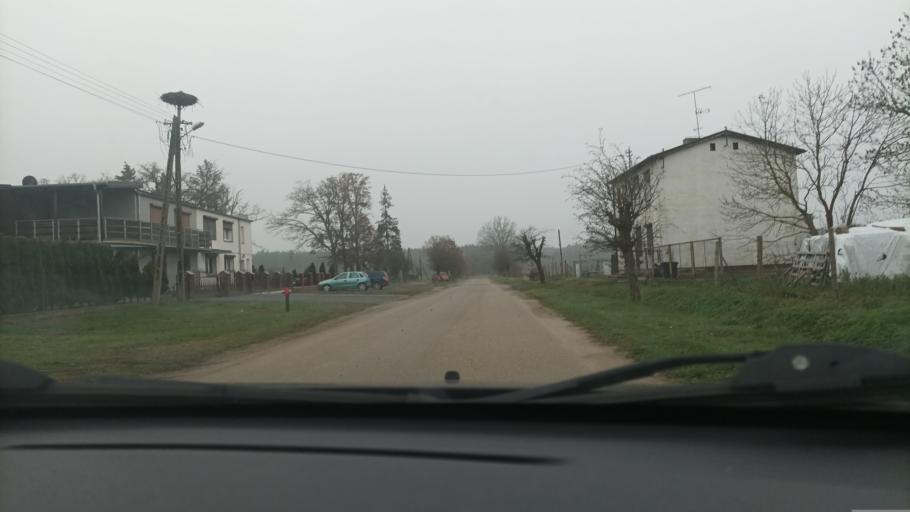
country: PL
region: Greater Poland Voivodeship
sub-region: Powiat obornicki
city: Ryczywol
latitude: 52.7562
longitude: 16.8159
